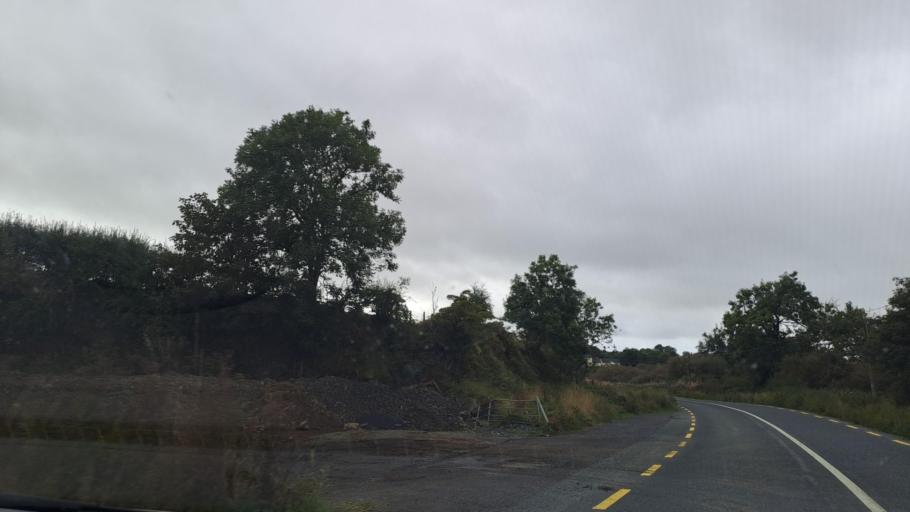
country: IE
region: Ulster
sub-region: An Cabhan
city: Bailieborough
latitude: 53.9568
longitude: -6.9415
